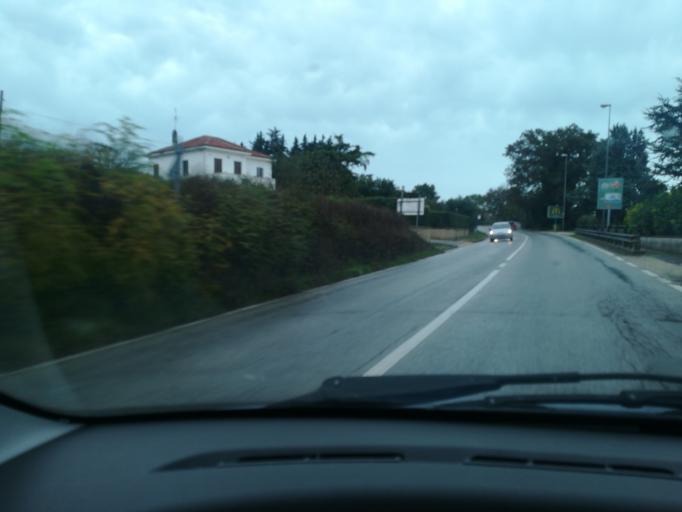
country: IT
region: The Marches
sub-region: Provincia di Macerata
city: Santa Maria Apparente
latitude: 43.2949
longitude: 13.6809
